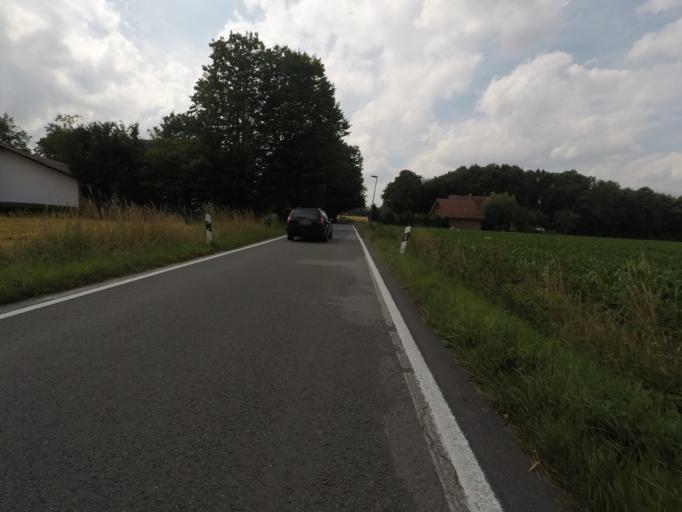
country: DE
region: North Rhine-Westphalia
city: Enger
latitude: 52.1616
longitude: 8.5549
